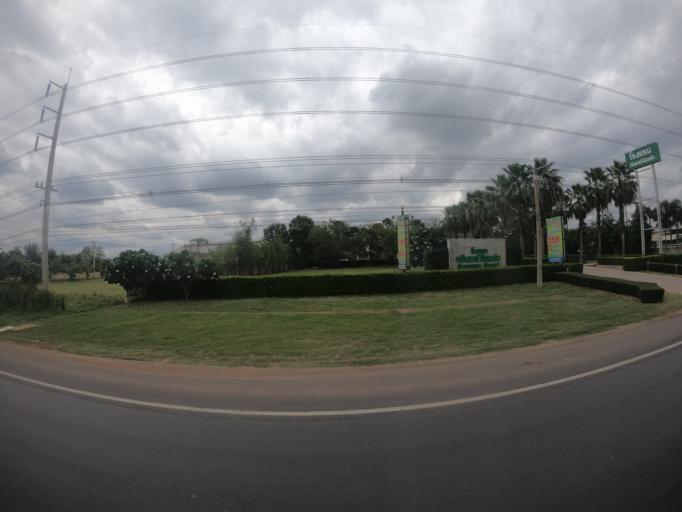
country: TH
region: Nakhon Ratchasima
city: Chok Chai
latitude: 14.7492
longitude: 102.2485
